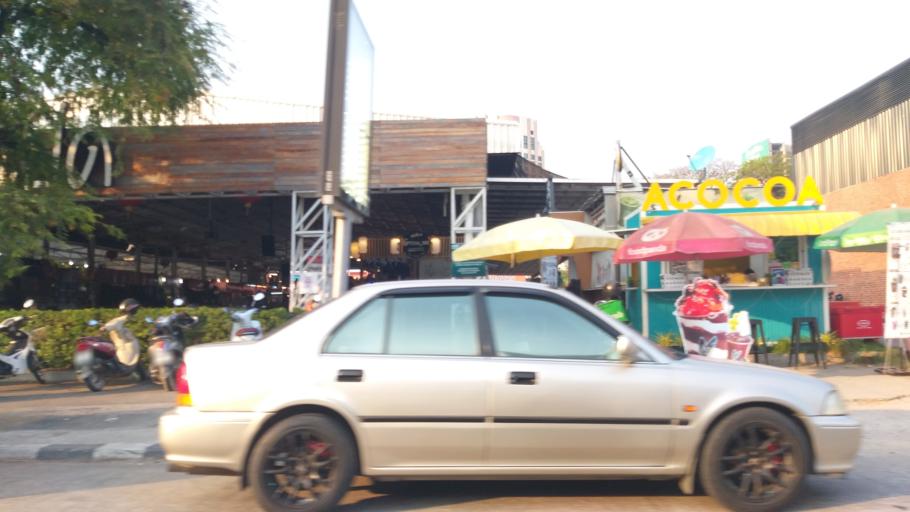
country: TH
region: Khon Kaen
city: Khon Kaen
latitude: 16.4261
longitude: 102.8300
